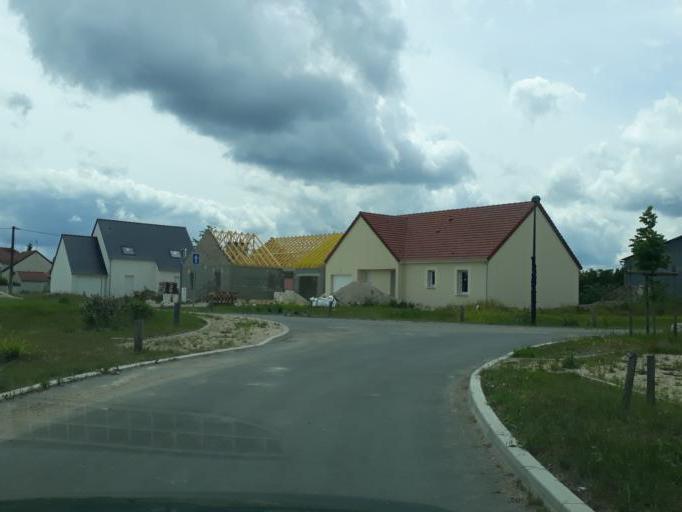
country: FR
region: Centre
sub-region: Departement du Loiret
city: Saint-Ay
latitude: 47.8560
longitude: 1.7446
